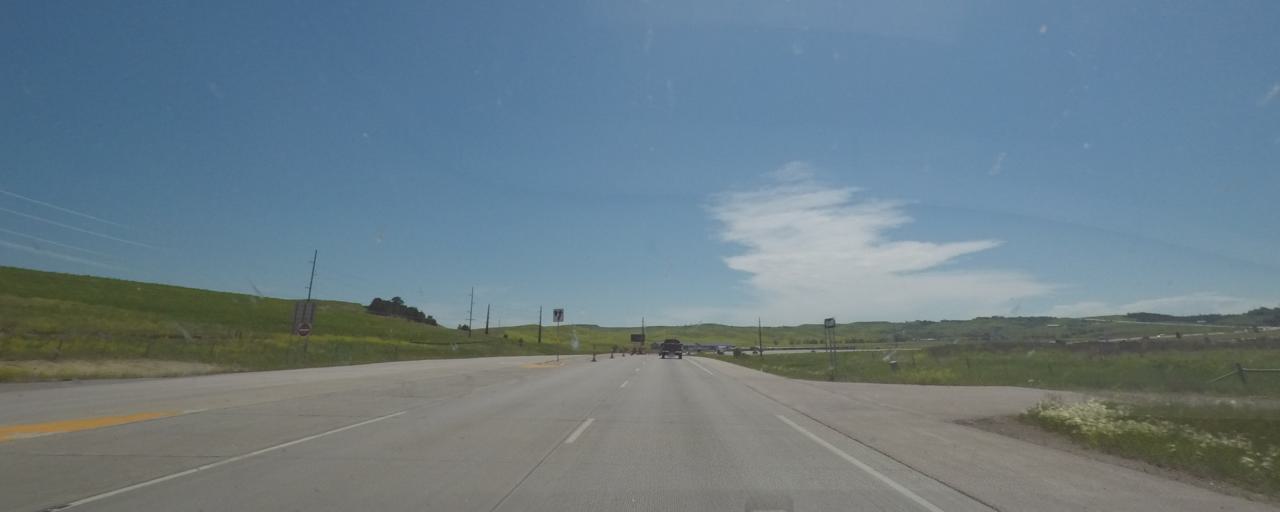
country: US
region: South Dakota
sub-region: Pennington County
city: Rapid City
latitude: 44.0350
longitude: -103.2033
